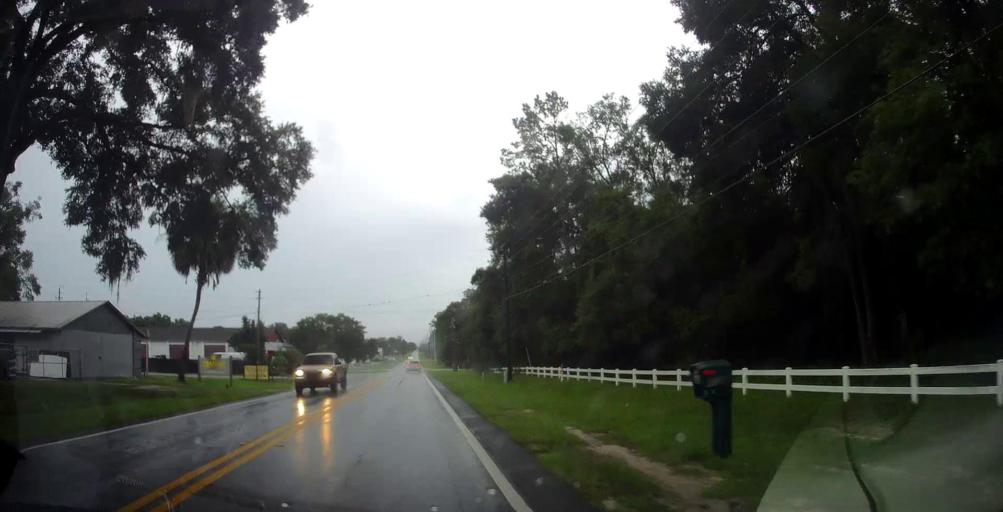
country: US
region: Florida
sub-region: Marion County
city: Ocala
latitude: 29.2329
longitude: -82.0869
